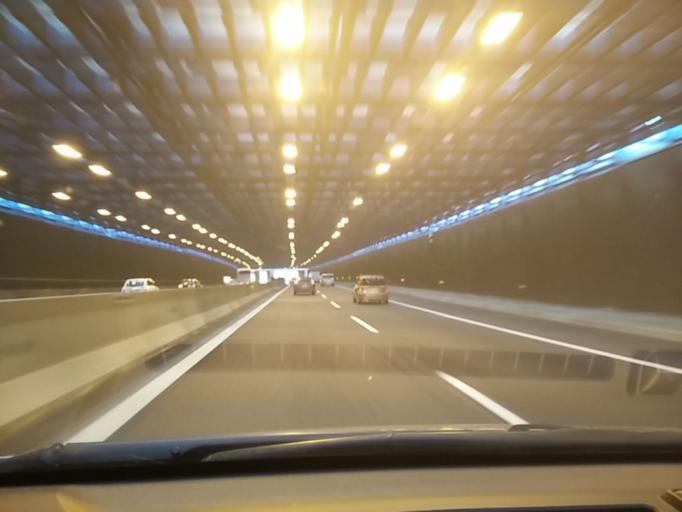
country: IT
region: Emilia-Romagna
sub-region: Provincia di Bologna
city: Quarto Inferiore
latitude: 44.5078
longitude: 11.3811
